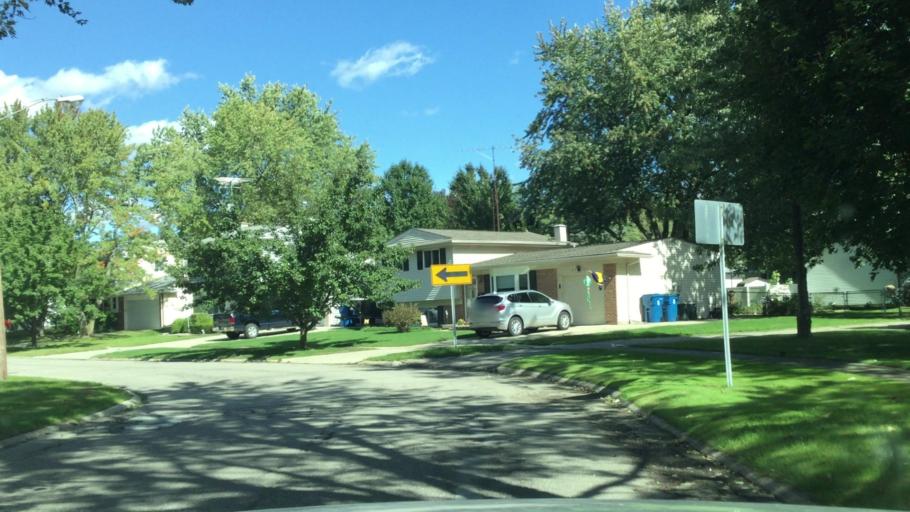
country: US
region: Michigan
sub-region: Genesee County
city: Swartz Creek
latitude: 42.9523
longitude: -83.8492
